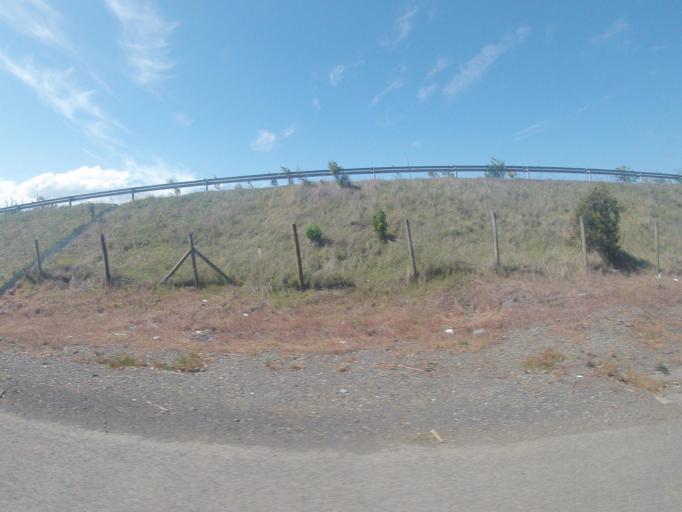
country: CL
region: Biobio
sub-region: Provincia de Biobio
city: Los Angeles
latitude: -37.4517
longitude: -72.4082
